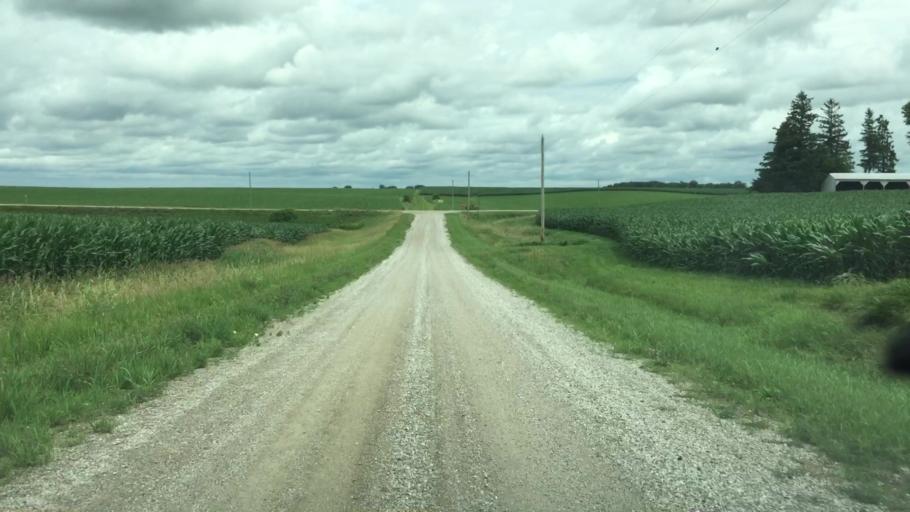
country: US
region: Iowa
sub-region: Jasper County
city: Monroe
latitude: 41.5788
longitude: -93.1208
